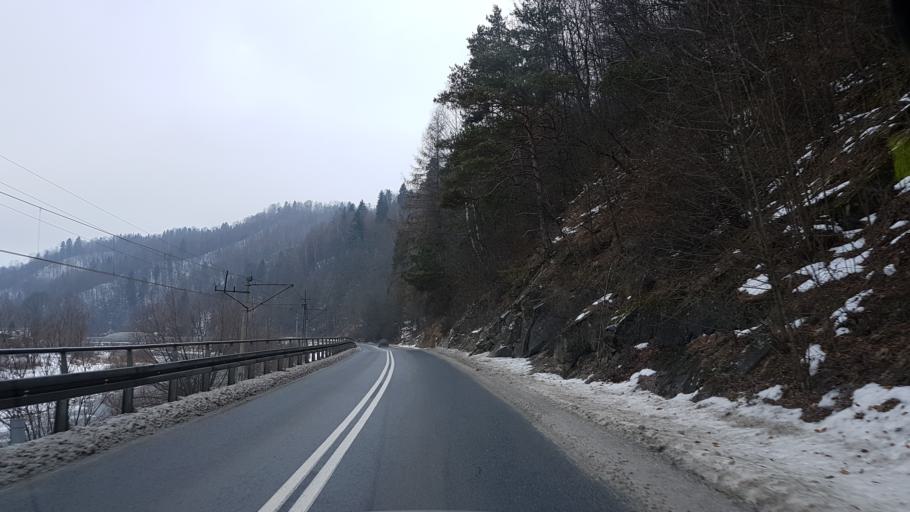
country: PL
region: Lesser Poland Voivodeship
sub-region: Powiat nowosadecki
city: Piwniczna-Zdroj
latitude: 49.4152
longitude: 20.7443
